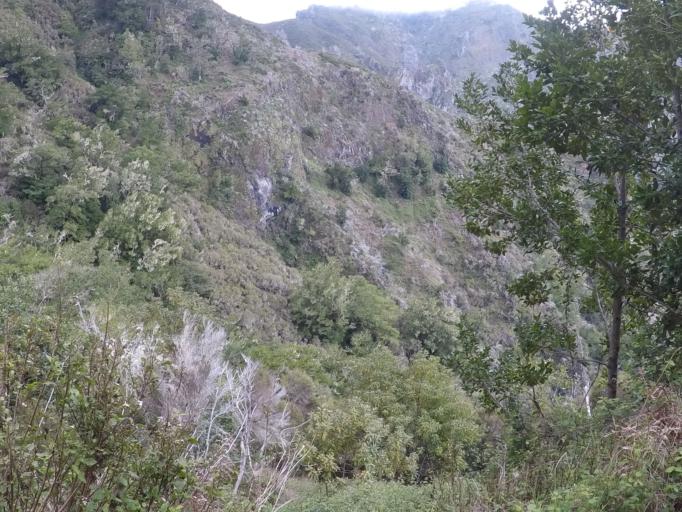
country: PT
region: Madeira
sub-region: Camara de Lobos
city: Curral das Freiras
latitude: 32.7359
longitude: -16.9962
